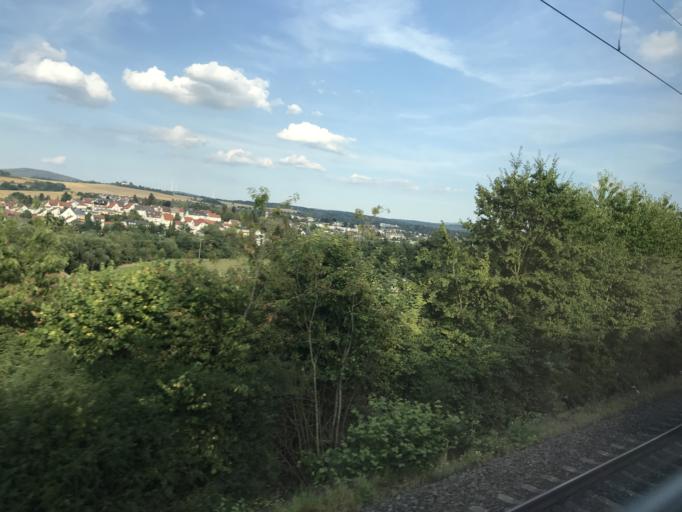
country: DE
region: Hesse
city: Bad Camberg
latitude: 50.3059
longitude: 8.2499
